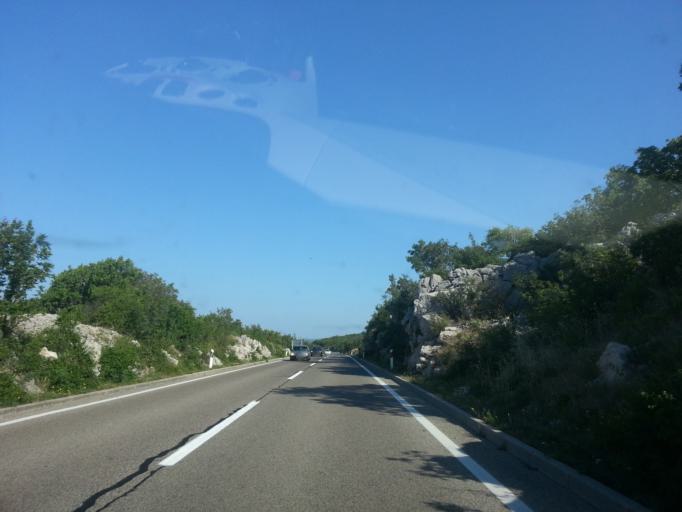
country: HR
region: Primorsko-Goranska
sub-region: Grad Crikvenica
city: Jadranovo
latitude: 45.2399
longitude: 14.6155
